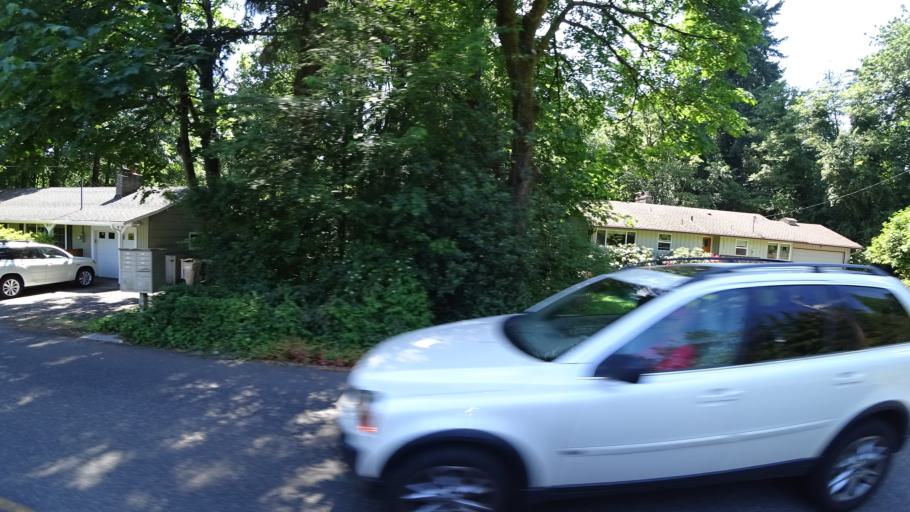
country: US
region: Oregon
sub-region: Clackamas County
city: Lake Oswego
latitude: 45.4241
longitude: -122.6954
